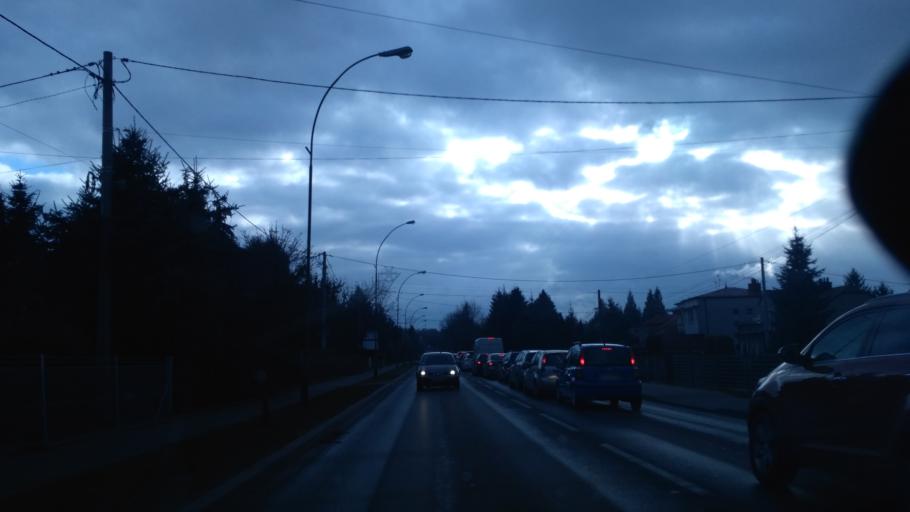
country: PL
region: Subcarpathian Voivodeship
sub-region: Powiat lancucki
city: Lancut
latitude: 50.0864
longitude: 22.2323
